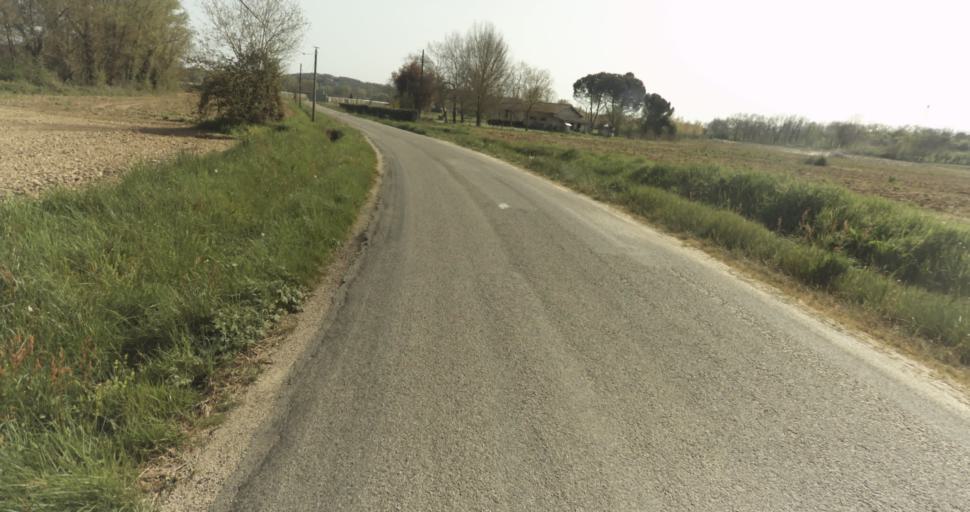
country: FR
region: Midi-Pyrenees
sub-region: Departement du Tarn-et-Garonne
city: Lafrancaise
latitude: 44.1395
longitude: 1.1749
